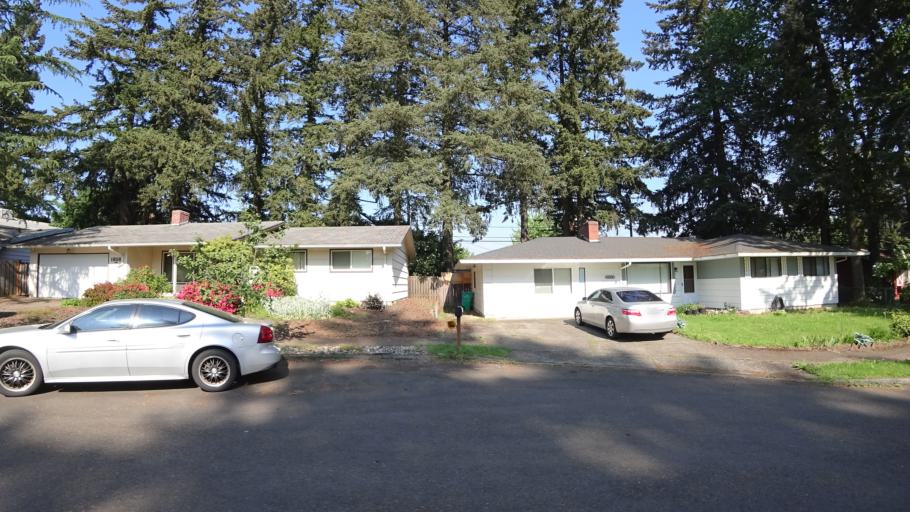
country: US
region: Oregon
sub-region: Multnomah County
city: Lents
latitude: 45.5092
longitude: -122.5086
